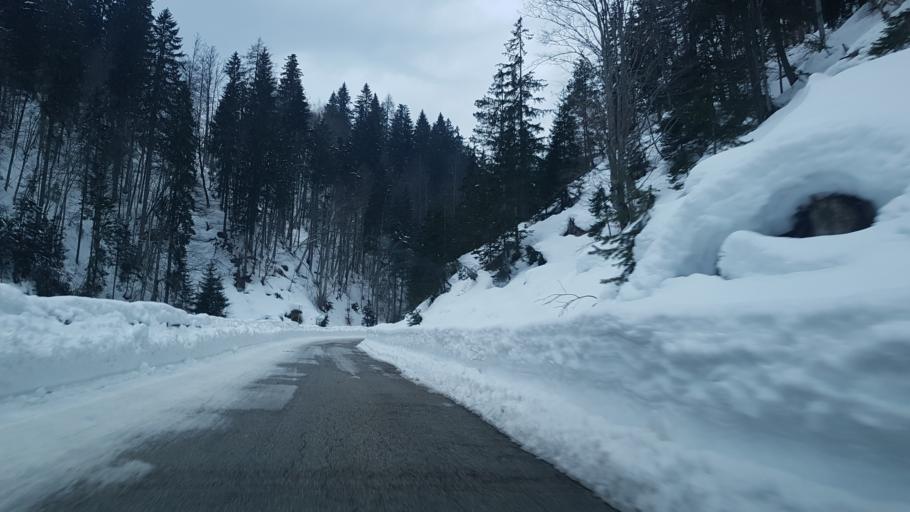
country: IT
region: Friuli Venezia Giulia
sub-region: Provincia di Udine
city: Malborghetto
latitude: 46.5292
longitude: 13.4727
